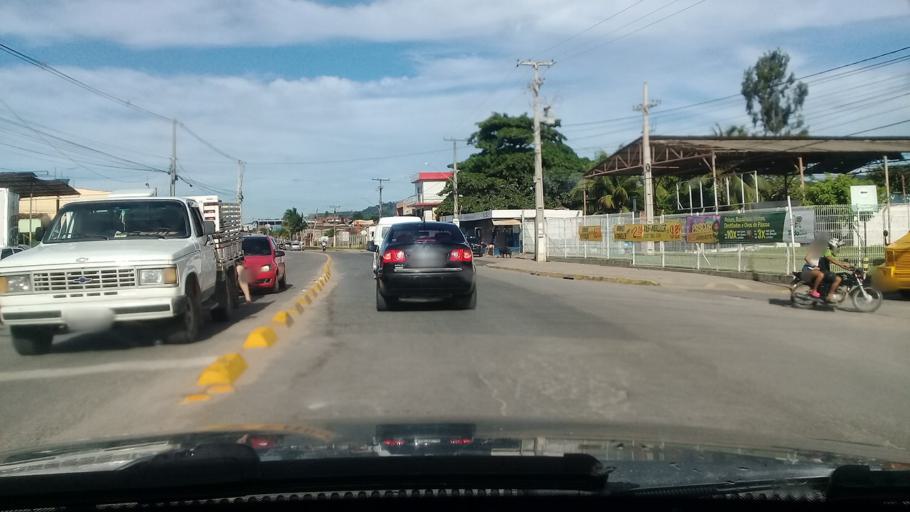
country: BR
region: Pernambuco
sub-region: Vitoria De Santo Antao
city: Vitoria de Santo Antao
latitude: -8.1139
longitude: -35.2850
